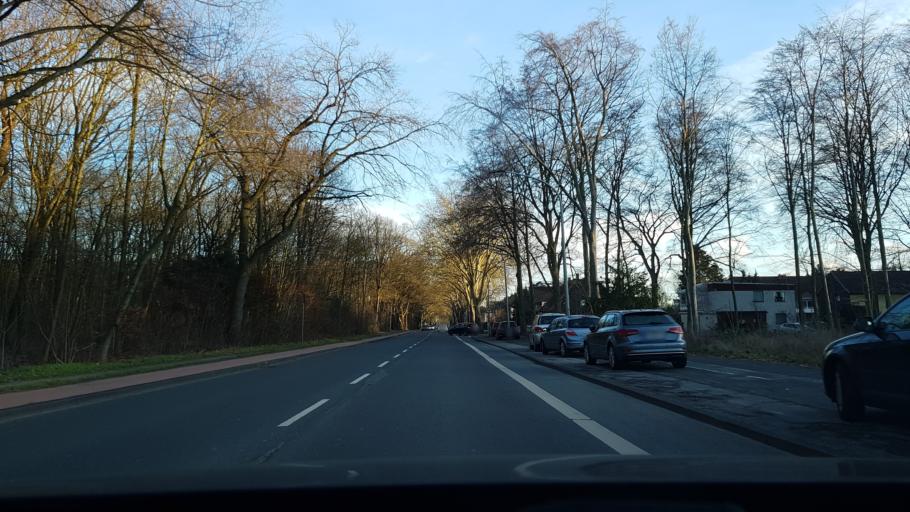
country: DE
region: North Rhine-Westphalia
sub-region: Regierungsbezirk Dusseldorf
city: Hochfeld
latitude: 51.3965
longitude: 6.7866
